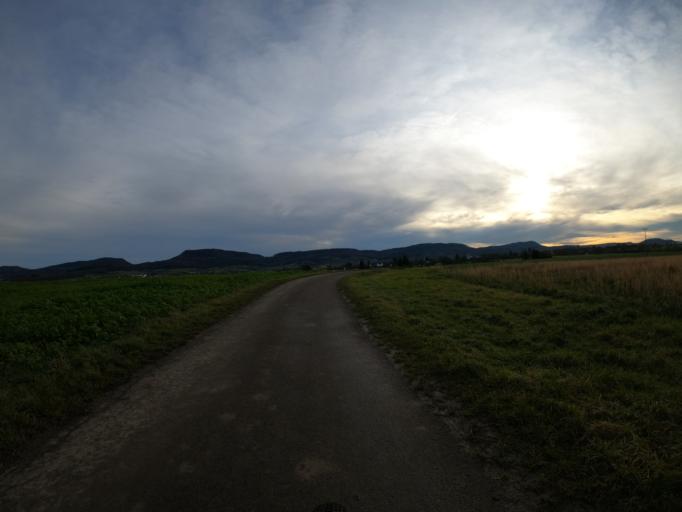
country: DE
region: Baden-Wuerttemberg
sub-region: Regierungsbezirk Stuttgart
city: Heiningen
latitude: 48.6720
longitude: 9.6498
